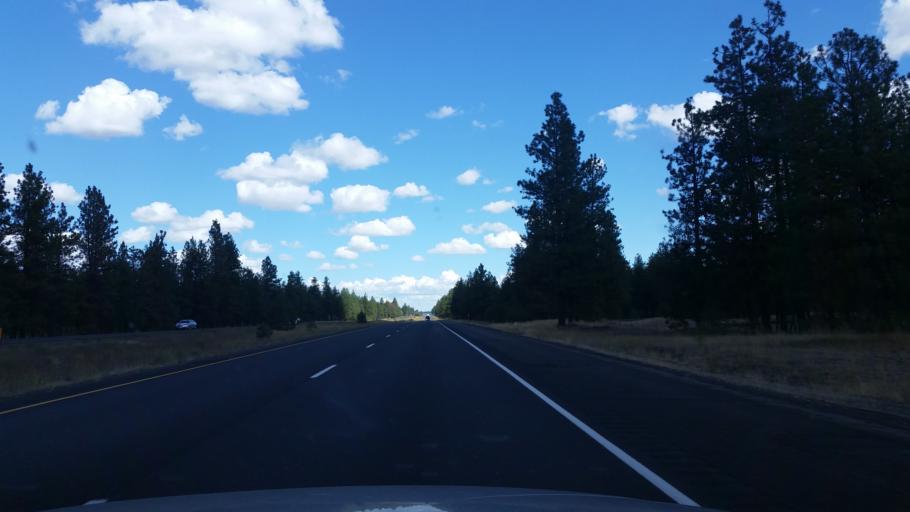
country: US
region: Washington
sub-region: Spokane County
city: Medical Lake
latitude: 47.4814
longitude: -117.7242
